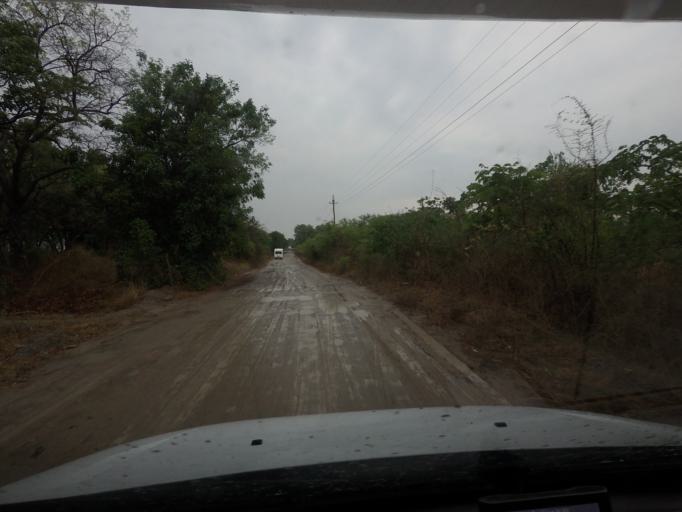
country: ZM
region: Western
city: Sesheke
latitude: -17.4870
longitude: 24.2850
